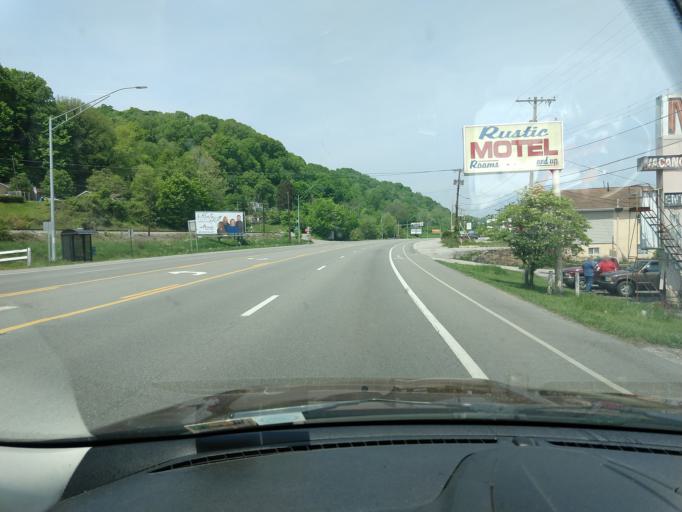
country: US
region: West Virginia
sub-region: Kanawha County
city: Dunbar
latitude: 38.3585
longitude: -81.7562
